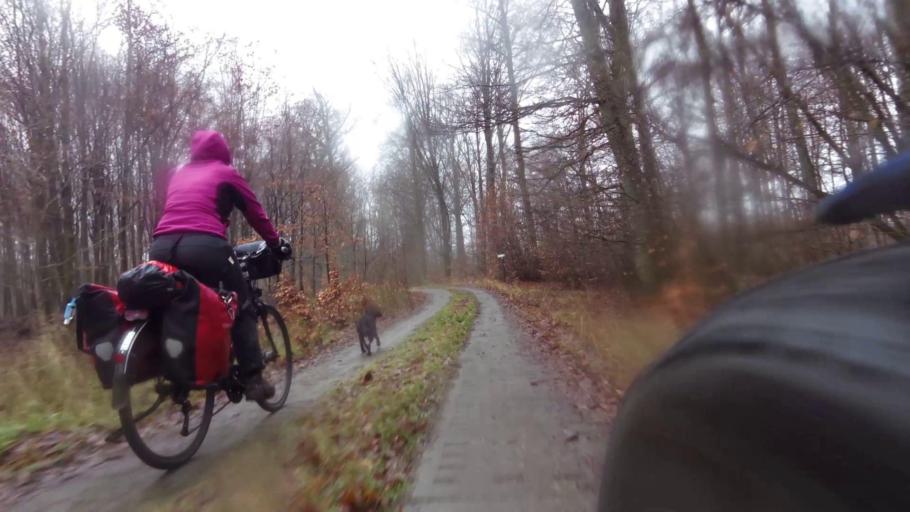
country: PL
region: West Pomeranian Voivodeship
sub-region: Powiat drawski
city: Czaplinek
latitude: 53.5936
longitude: 16.2699
